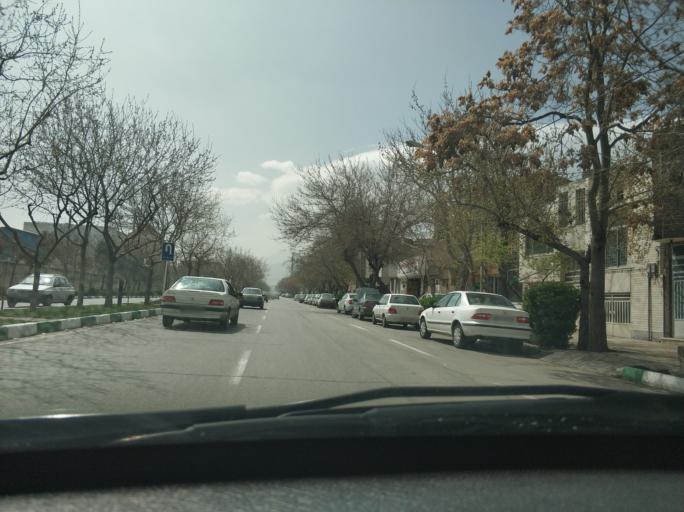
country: IR
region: Razavi Khorasan
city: Mashhad
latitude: 36.2796
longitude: 59.5770
